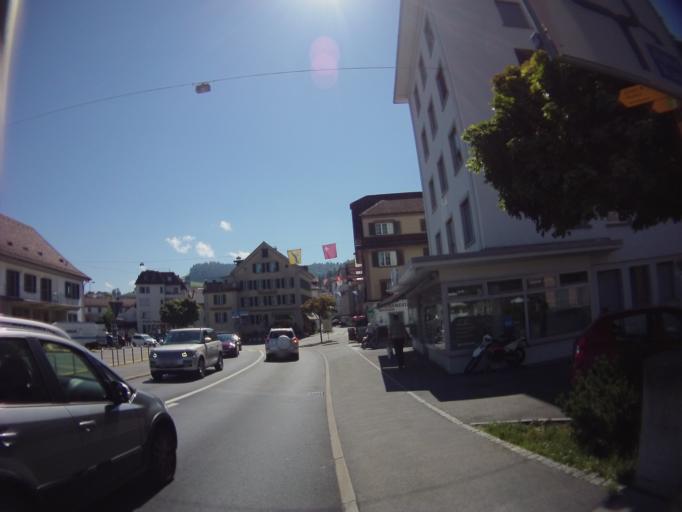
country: CH
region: Schwyz
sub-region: Bezirk Einsiedeln
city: Einsiedeln
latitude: 47.1279
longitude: 8.7435
